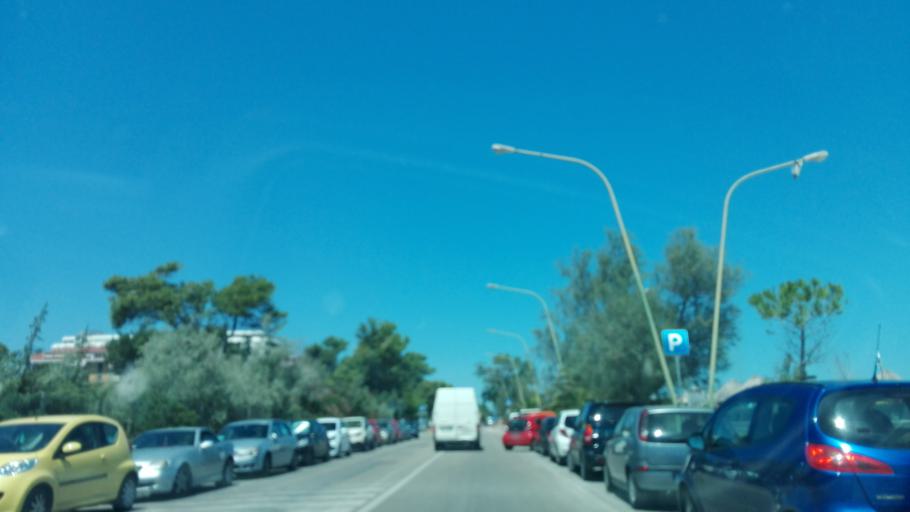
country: IT
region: Abruzzo
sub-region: Provincia di Pescara
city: Villa Raspa
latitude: 42.4923
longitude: 14.1865
